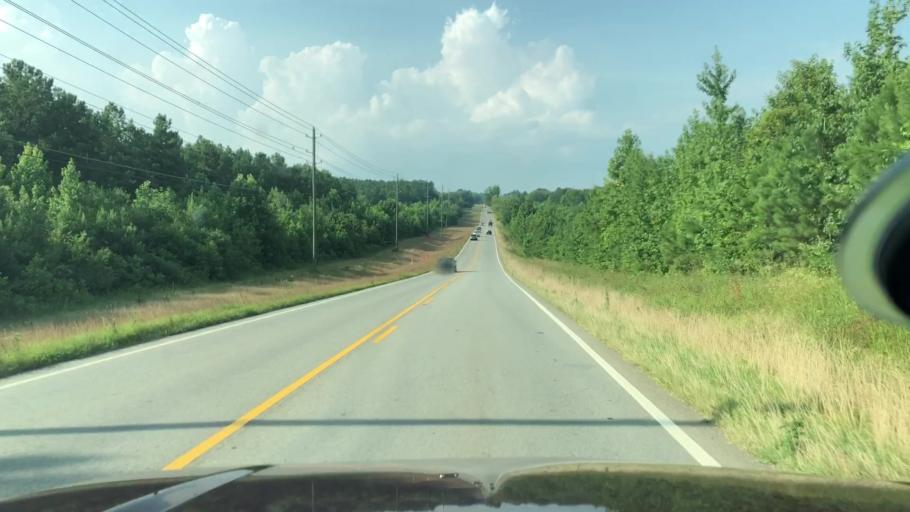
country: US
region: Georgia
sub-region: Paulding County
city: Dallas
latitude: 33.9962
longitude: -84.8693
